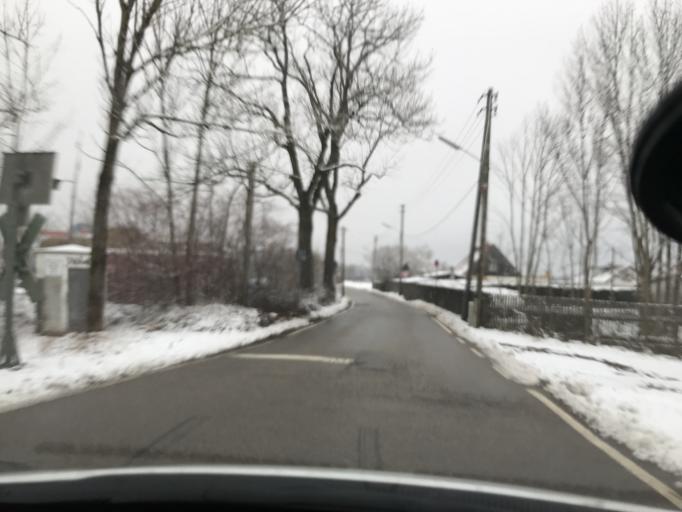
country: DE
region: Bavaria
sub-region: Upper Bavaria
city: Neubiberg
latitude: 48.0850
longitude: 11.6491
